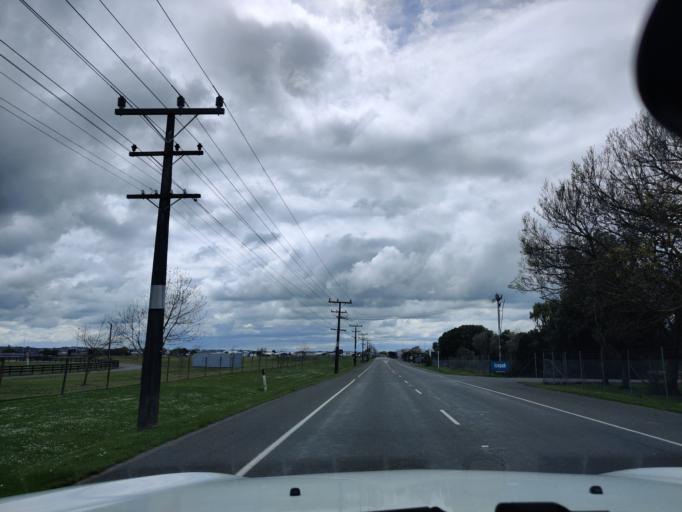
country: NZ
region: Manawatu-Wanganui
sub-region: Palmerston North City
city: Palmerston North
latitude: -40.2375
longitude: 175.5626
